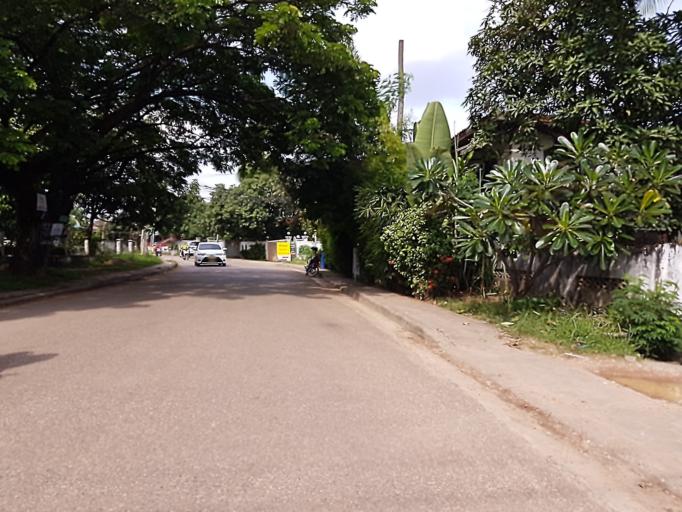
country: LA
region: Vientiane
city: Vientiane
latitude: 17.9475
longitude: 102.6242
